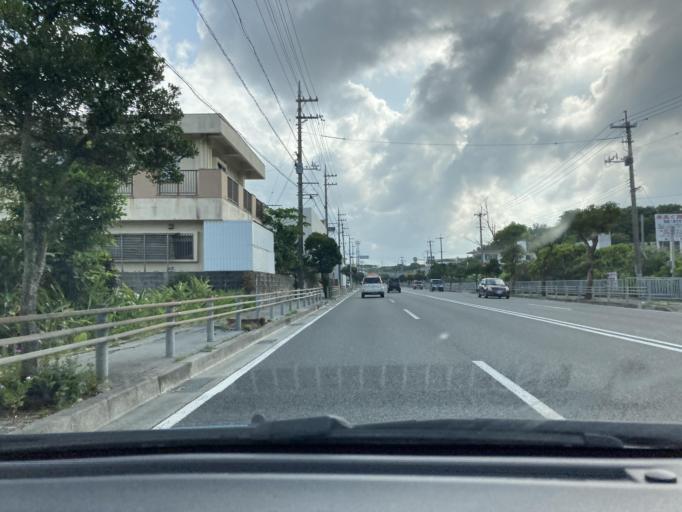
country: JP
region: Okinawa
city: Ginowan
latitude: 26.2407
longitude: 127.7781
